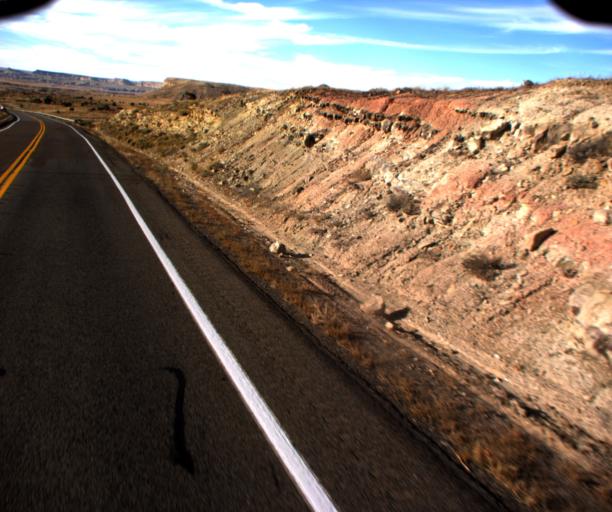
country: US
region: New Mexico
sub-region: San Juan County
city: Shiprock
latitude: 36.9134
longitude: -109.0752
